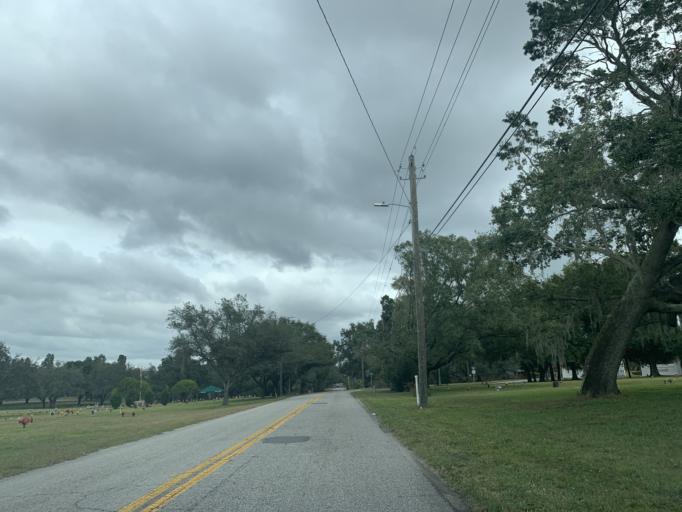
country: US
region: Florida
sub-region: Hillsborough County
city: East Lake-Orient Park
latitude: 27.9793
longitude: -82.4068
